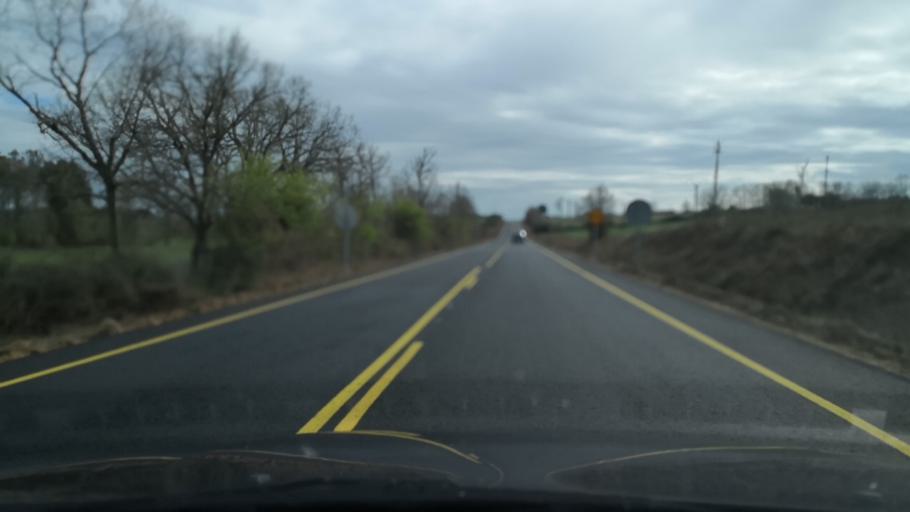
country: ES
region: Castille and Leon
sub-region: Provincia de Salamanca
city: Robleda
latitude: 40.3658
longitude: -6.6209
